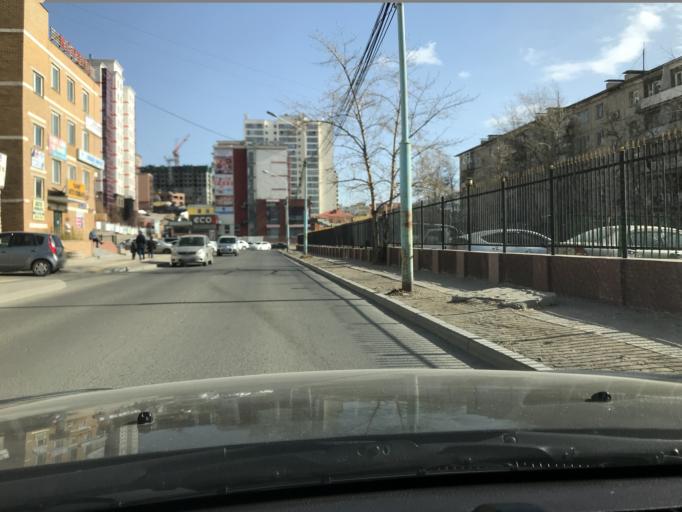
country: MN
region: Ulaanbaatar
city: Ulaanbaatar
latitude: 47.9213
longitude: 106.9511
